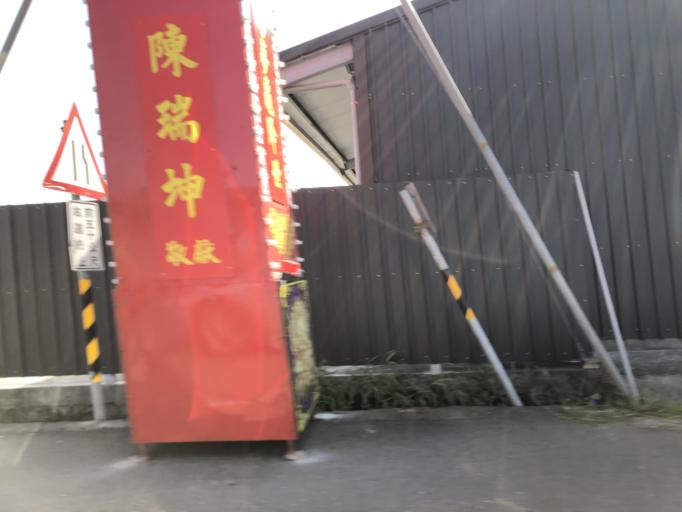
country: TW
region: Taiwan
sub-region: Tainan
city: Tainan
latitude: 23.0241
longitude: 120.2900
